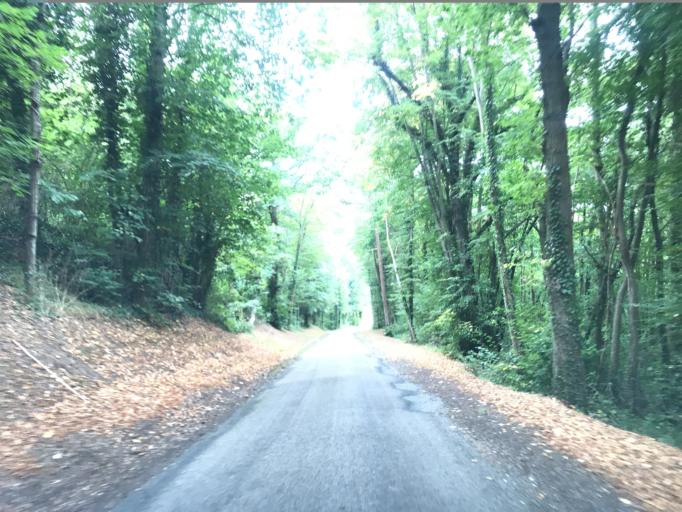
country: FR
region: Haute-Normandie
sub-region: Departement de l'Eure
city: Houlbec-Cocherel
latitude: 49.0613
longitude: 1.3361
